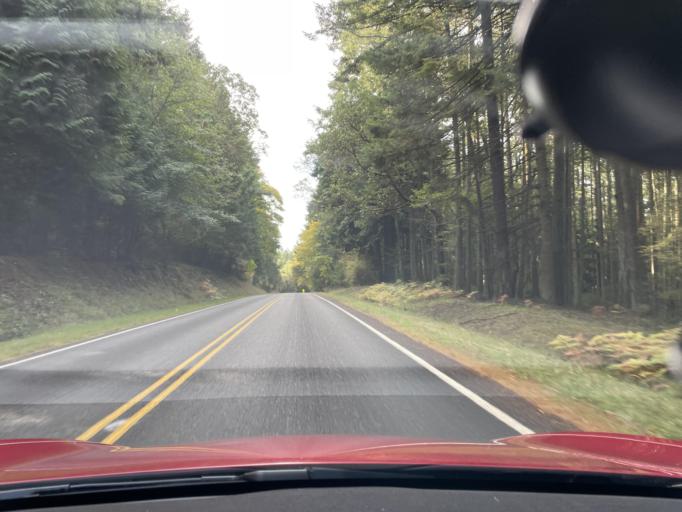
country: US
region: Washington
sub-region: San Juan County
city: Friday Harbor
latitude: 48.5874
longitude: -123.1412
